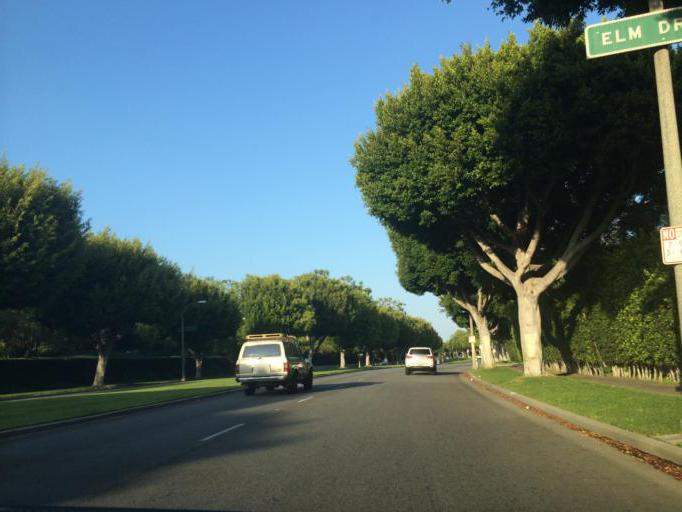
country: US
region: California
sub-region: Los Angeles County
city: Beverly Hills
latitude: 34.0865
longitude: -118.4052
